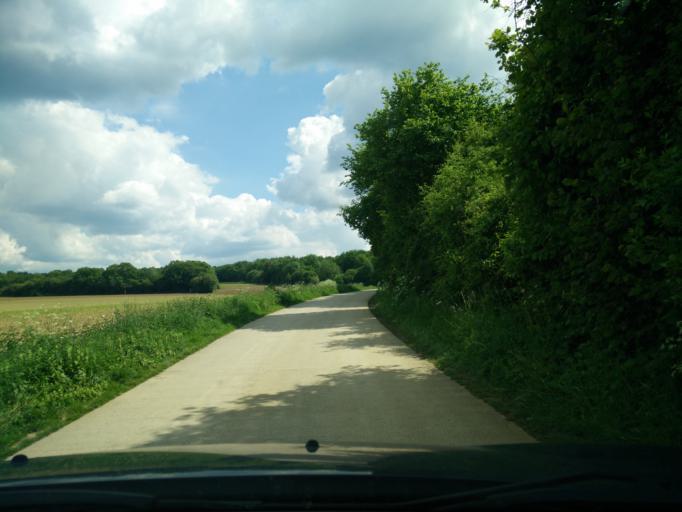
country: BE
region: Wallonia
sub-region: Province de Namur
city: Couvin
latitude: 50.0923
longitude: 4.6057
